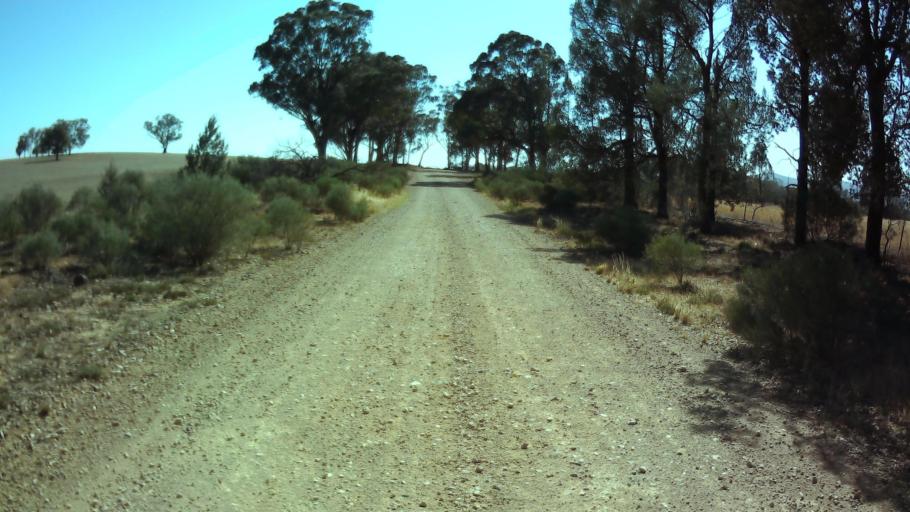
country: AU
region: New South Wales
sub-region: Weddin
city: Grenfell
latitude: -33.9025
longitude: 147.8652
